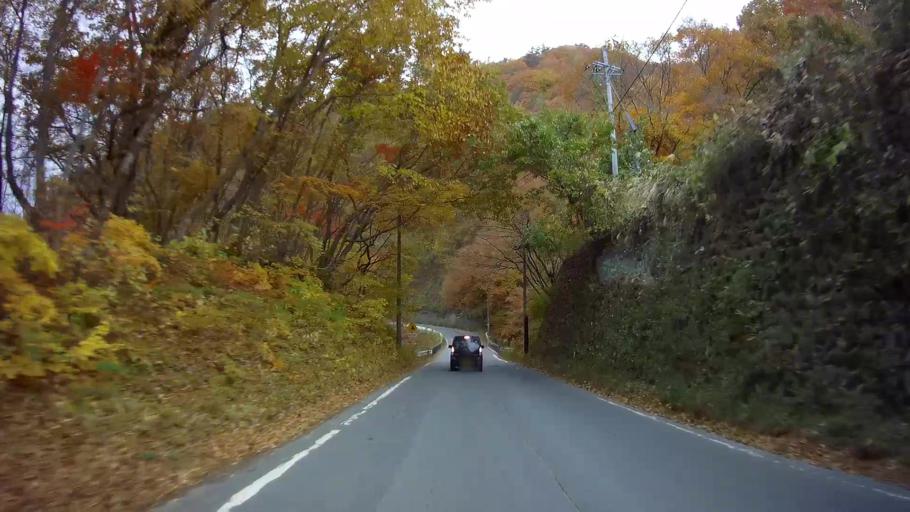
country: JP
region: Gunma
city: Nakanojomachi
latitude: 36.6258
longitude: 138.6479
